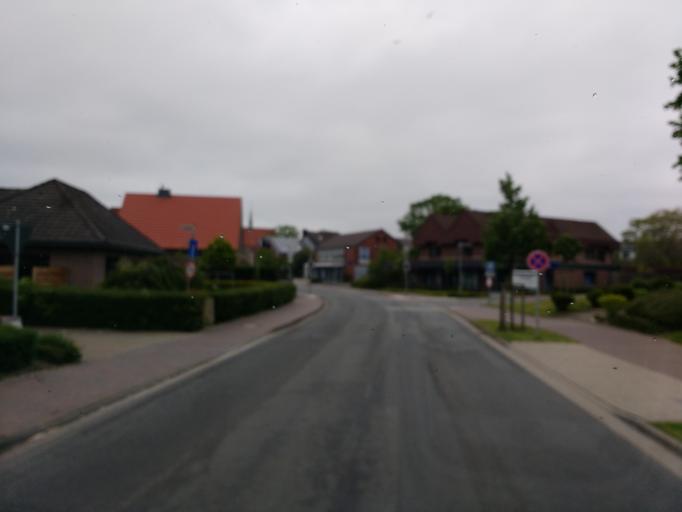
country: DE
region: Lower Saxony
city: Jever
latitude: 53.6605
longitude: 7.9165
